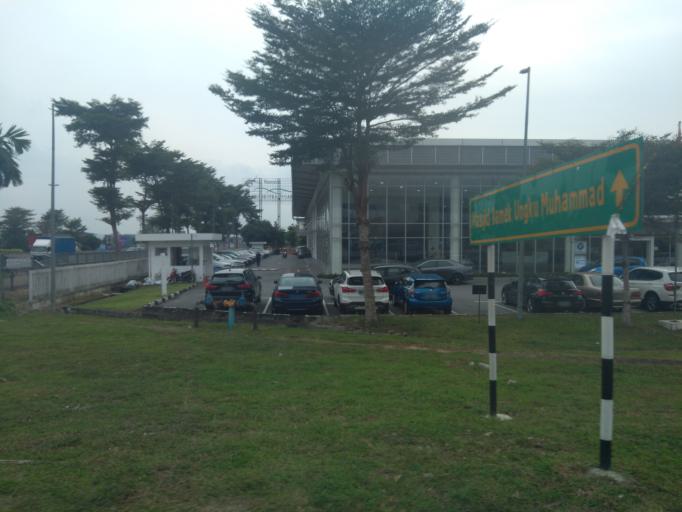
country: MY
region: Johor
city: Johor Bahru
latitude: 1.4860
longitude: 103.7164
